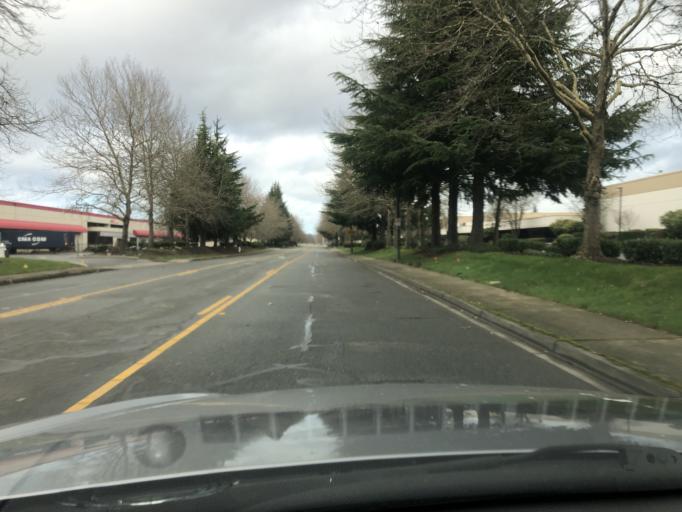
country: US
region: Washington
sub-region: King County
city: Kent
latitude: 47.4199
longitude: -122.2439
